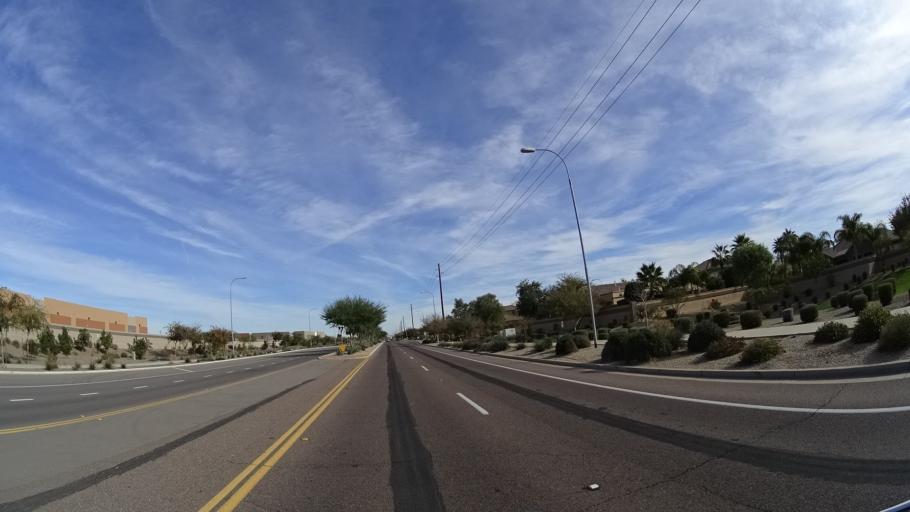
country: US
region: Arizona
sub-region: Maricopa County
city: Chandler
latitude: 33.2628
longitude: -111.7959
